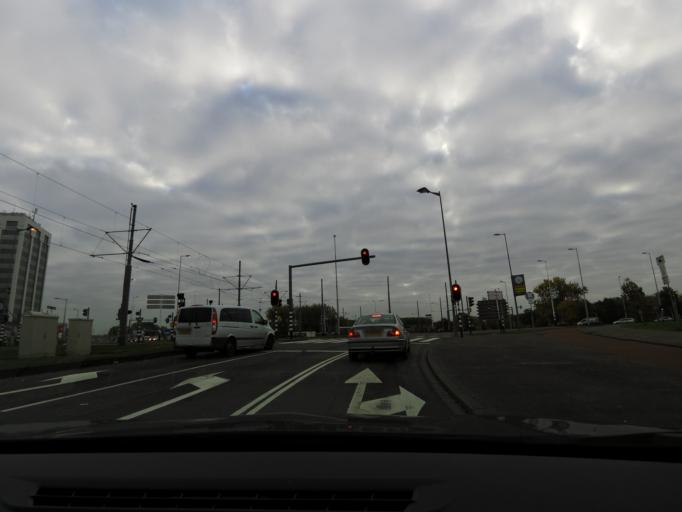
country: NL
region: South Holland
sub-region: Gemeente Rotterdam
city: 's-Gravenland
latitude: 51.8949
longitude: 4.5278
